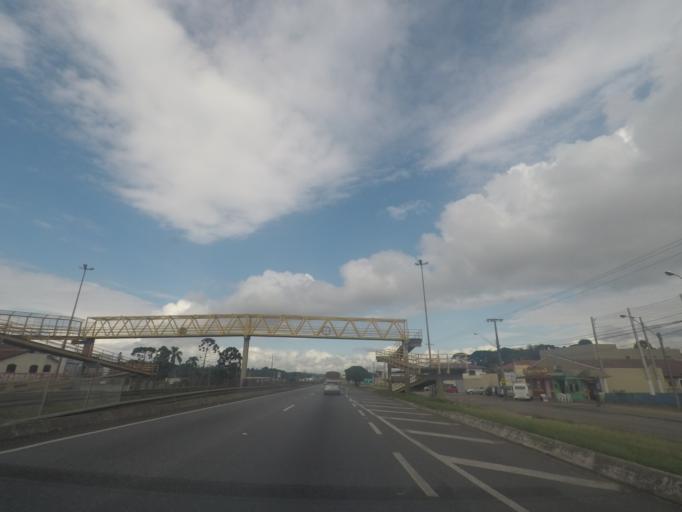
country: BR
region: Parana
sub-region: Piraquara
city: Piraquara
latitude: -25.5252
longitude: -49.0977
